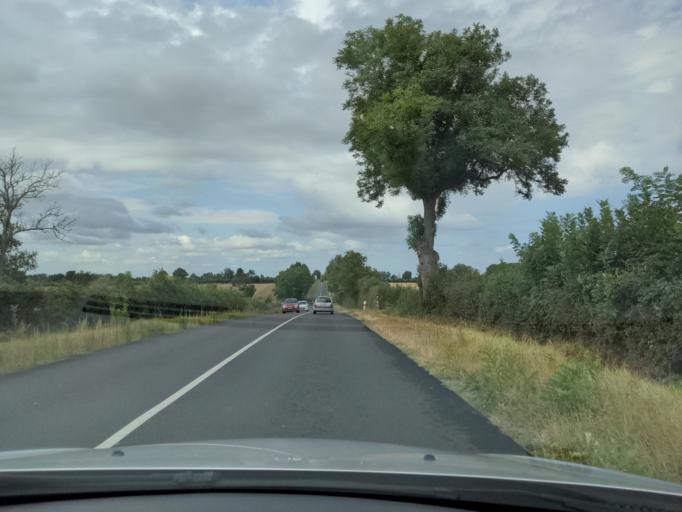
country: FR
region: Auvergne
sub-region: Departement de l'Allier
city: Neuvy
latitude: 46.5553
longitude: 3.2812
